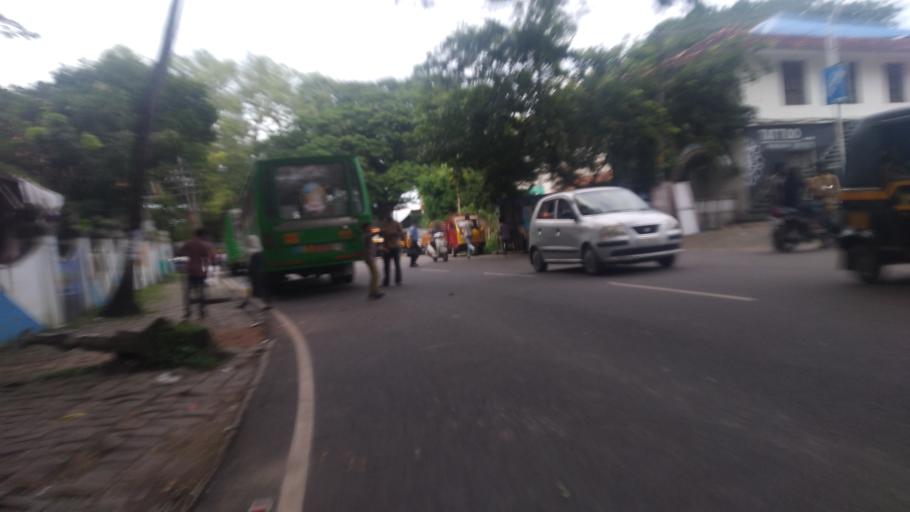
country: IN
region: Kerala
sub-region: Ernakulam
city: Cochin
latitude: 9.9680
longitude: 76.2444
